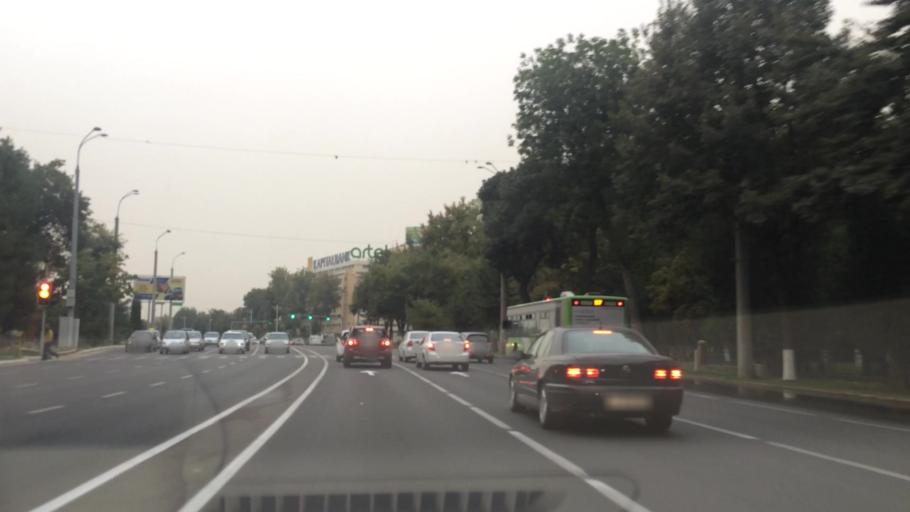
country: UZ
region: Toshkent Shahri
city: Tashkent
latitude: 41.3038
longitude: 69.2678
